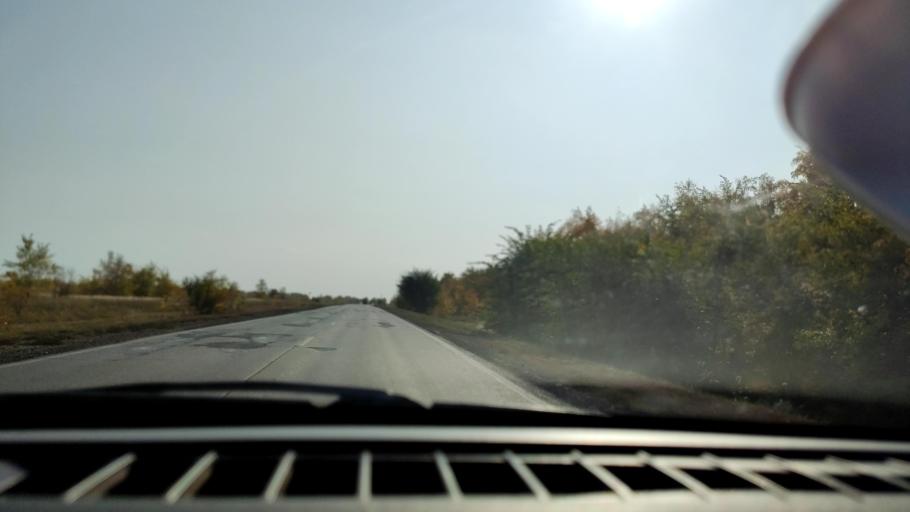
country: RU
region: Samara
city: Smyshlyayevka
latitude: 53.1250
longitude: 50.3684
